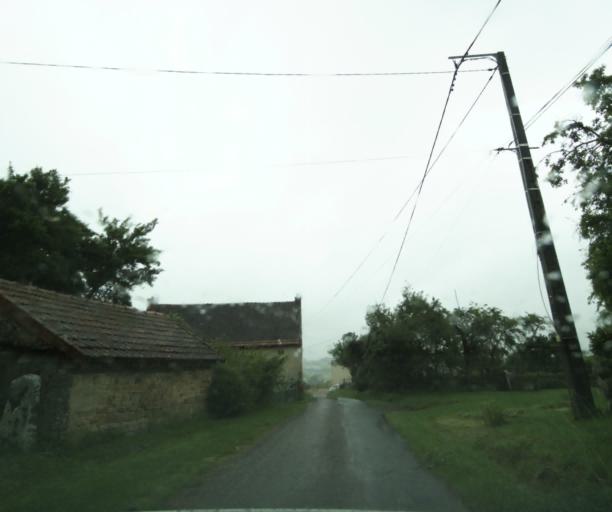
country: FR
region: Bourgogne
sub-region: Departement de Saone-et-Loire
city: Ciry-le-Noble
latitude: 46.5388
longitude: 4.3584
